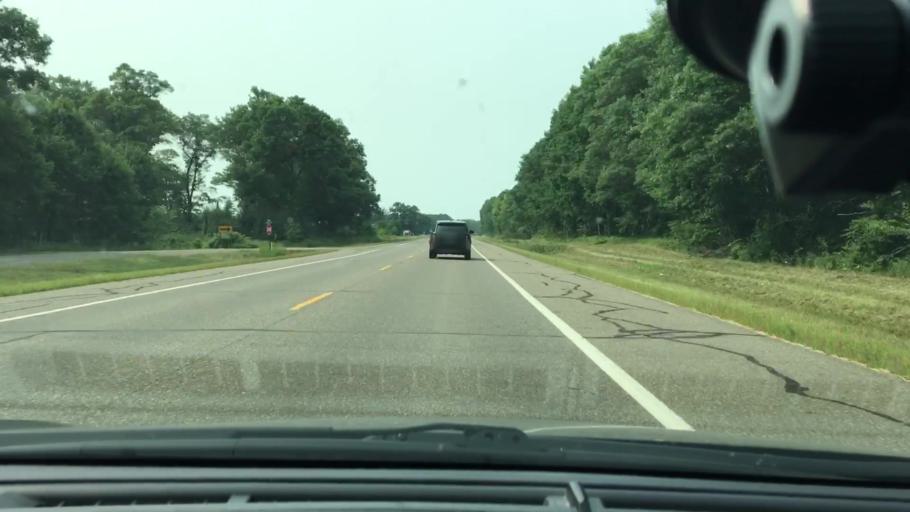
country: US
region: Minnesota
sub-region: Crow Wing County
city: Breezy Point
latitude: 46.4928
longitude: -94.1505
